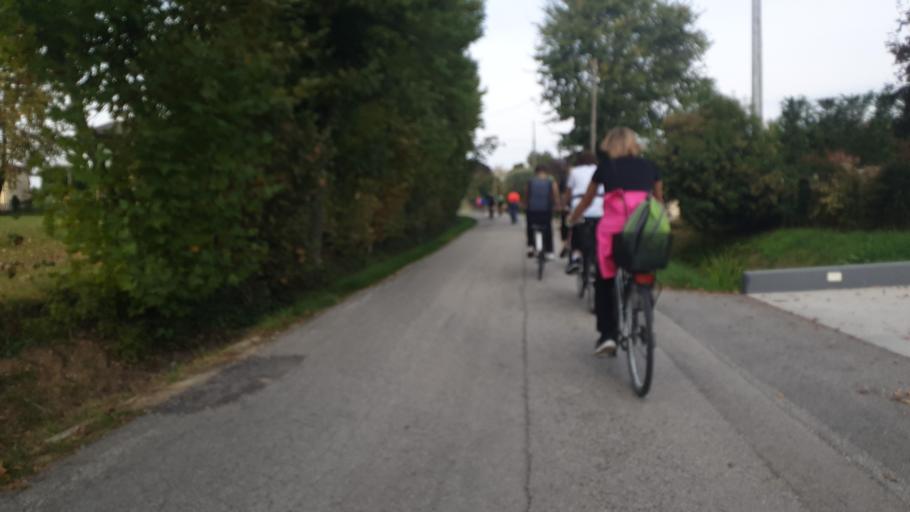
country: IT
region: Veneto
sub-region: Provincia di Padova
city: Cervarese Santa Croce
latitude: 45.4166
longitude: 11.6995
